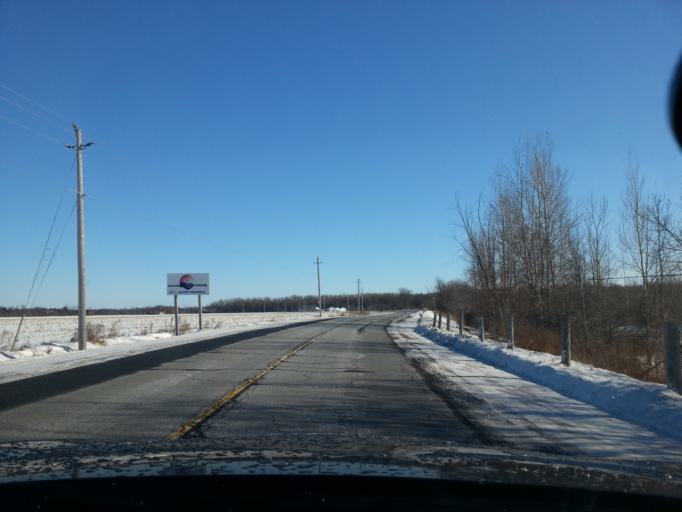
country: CA
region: Ontario
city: Bourget
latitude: 45.2546
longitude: -75.3918
